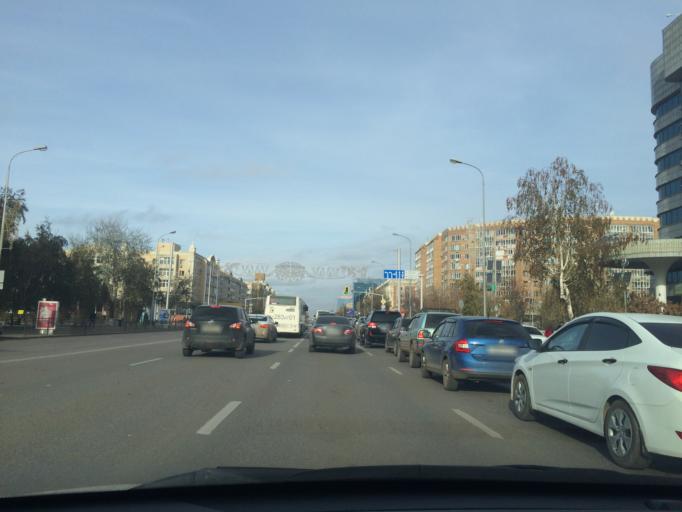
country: KZ
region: Astana Qalasy
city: Astana
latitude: 51.1645
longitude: 71.4277
